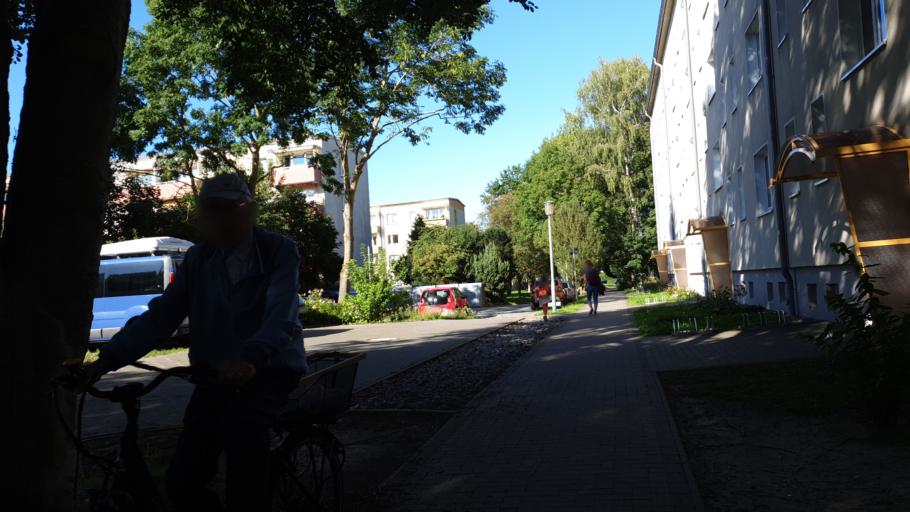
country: DE
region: Mecklenburg-Vorpommern
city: Stralsund
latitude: 54.3309
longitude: 13.0748
